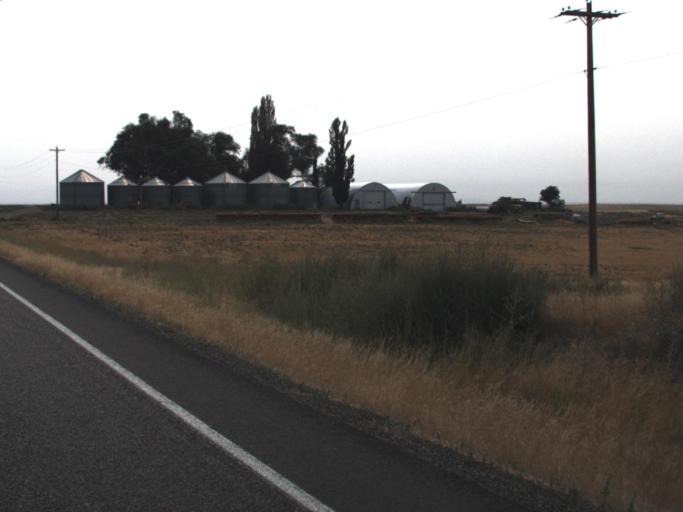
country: US
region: Oregon
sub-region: Morrow County
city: Irrigon
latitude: 46.0729
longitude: -119.6021
